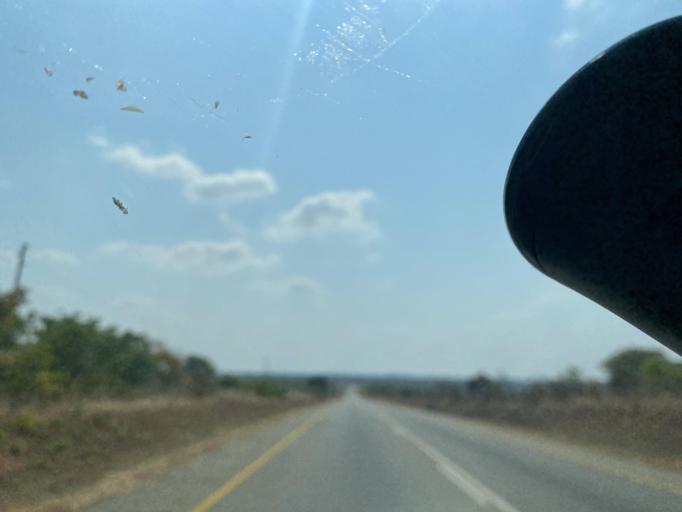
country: ZM
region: Lusaka
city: Chongwe
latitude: -15.5300
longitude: 28.6248
